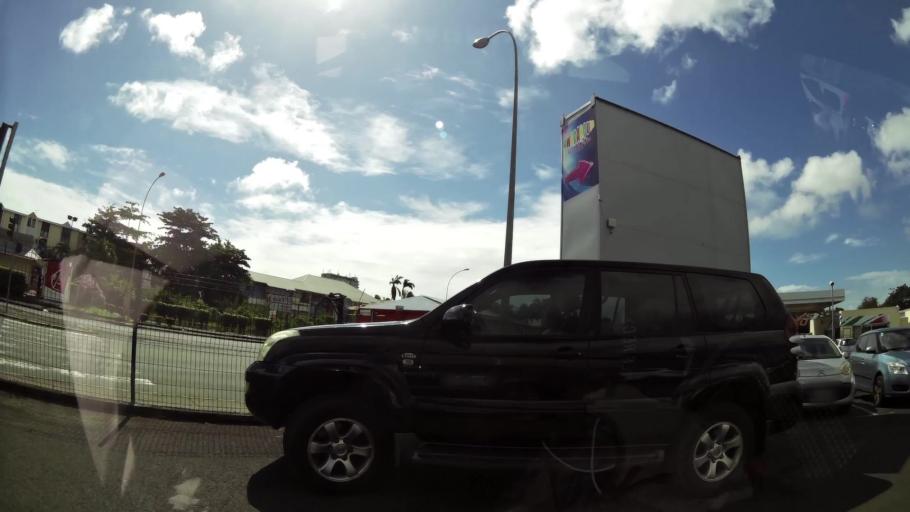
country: GP
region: Guadeloupe
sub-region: Guadeloupe
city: Pointe-a-Pitre
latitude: 16.2540
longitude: -61.5235
